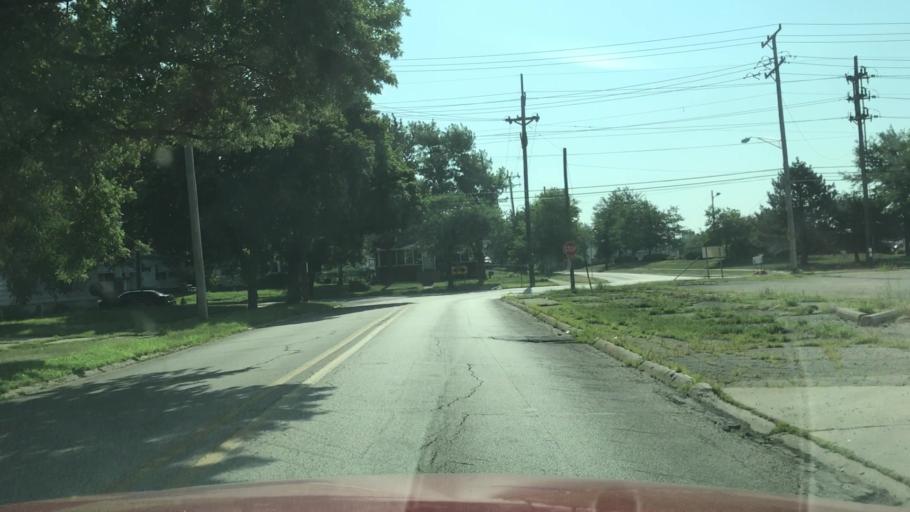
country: US
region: Illinois
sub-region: Winnebago County
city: Rockford
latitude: 42.2411
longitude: -89.0779
